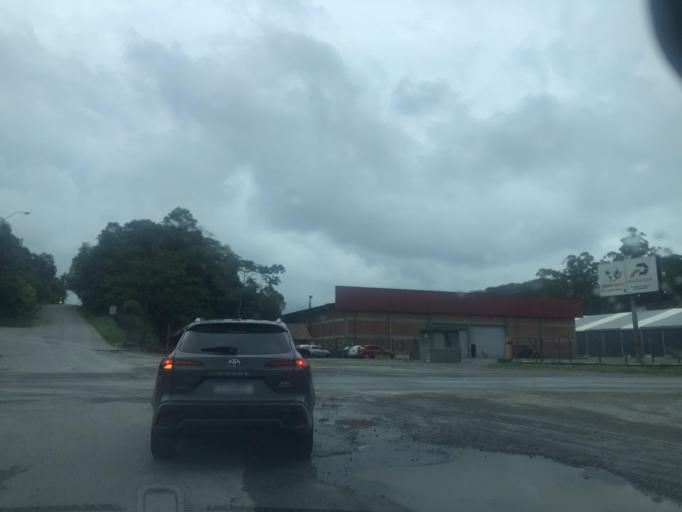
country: BR
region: Santa Catarina
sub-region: Sao Francisco Do Sul
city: Sao Francisco do Sul
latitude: -26.2404
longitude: -48.6176
